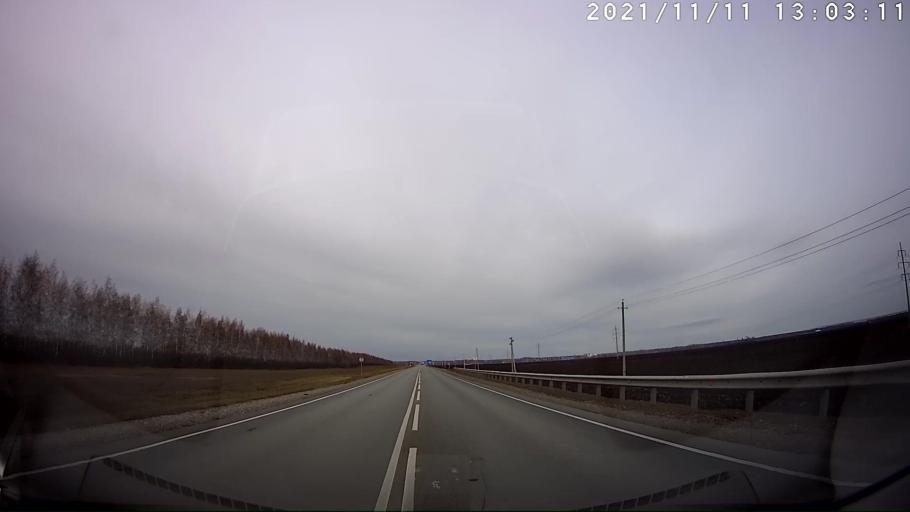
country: RU
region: Ulyanovsk
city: Isheyevka
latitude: 54.4055
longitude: 48.1772
